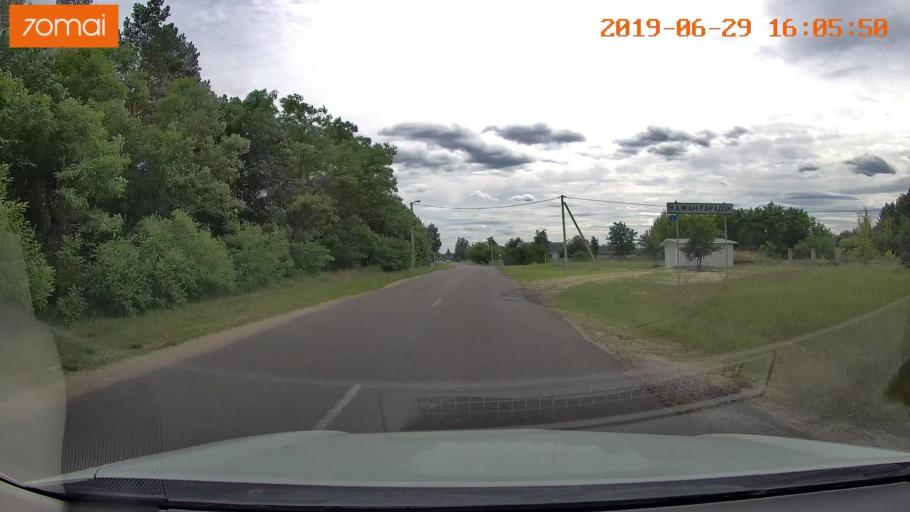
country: BY
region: Brest
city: Luninyets
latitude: 52.2134
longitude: 27.0168
